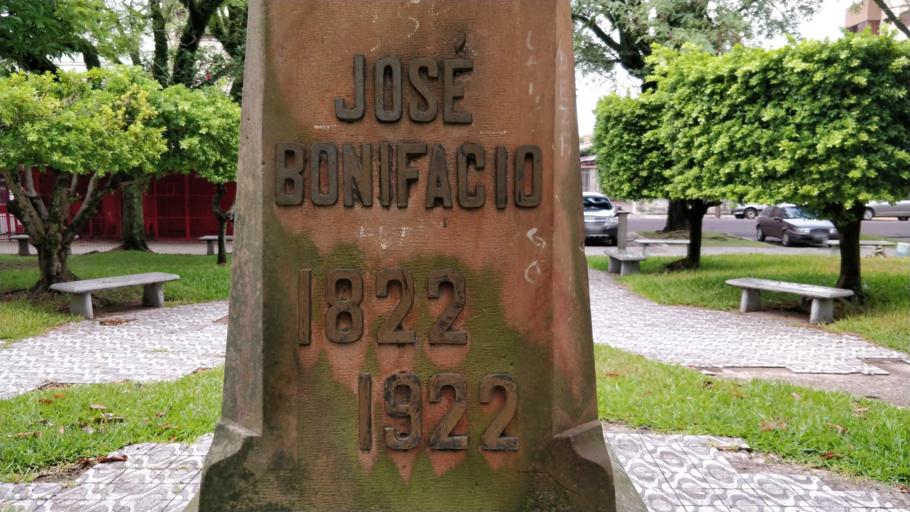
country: BR
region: Rio Grande do Sul
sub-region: Itaqui
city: Itaqui
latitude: -29.1222
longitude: -56.5563
